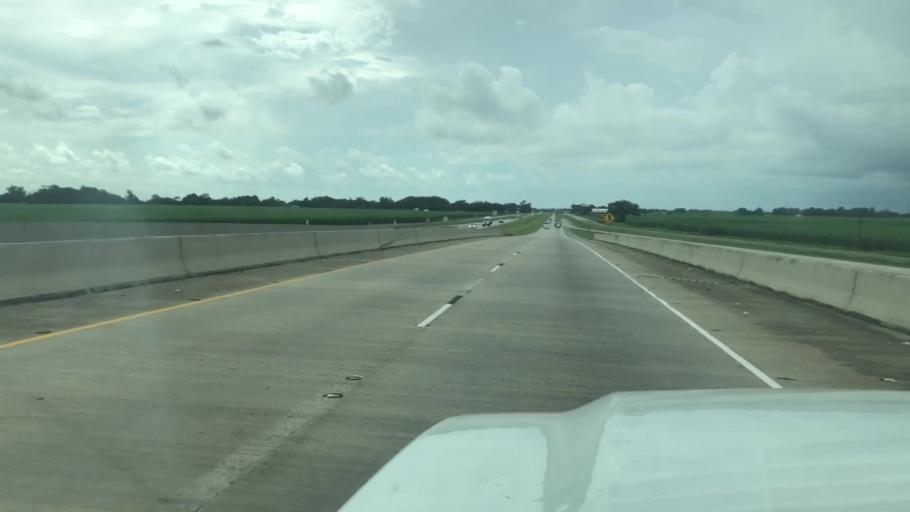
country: US
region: Louisiana
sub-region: Iberia Parish
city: Jeanerette
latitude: 29.9204
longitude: -91.7295
